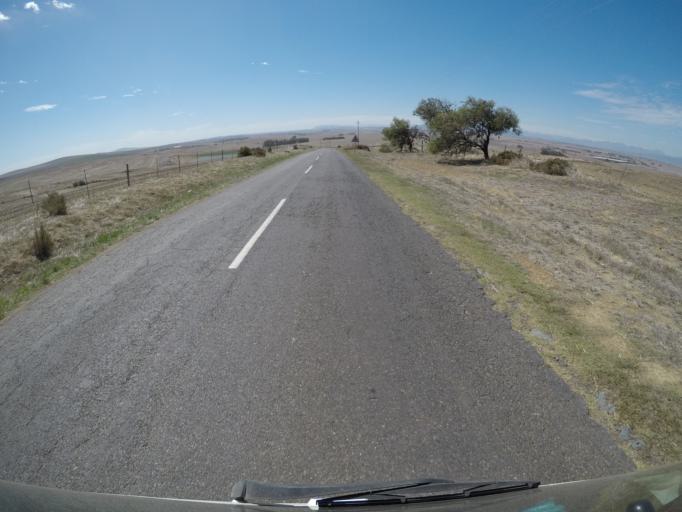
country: ZA
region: Western Cape
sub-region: City of Cape Town
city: Sunset Beach
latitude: -33.7087
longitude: 18.5840
